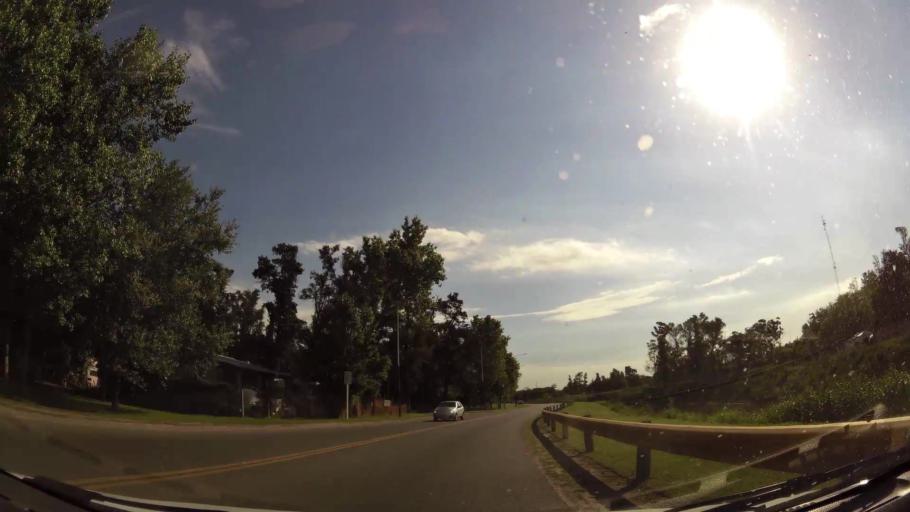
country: AR
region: Buenos Aires
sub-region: Partido de Merlo
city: Merlo
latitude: -34.6544
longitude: -58.7491
